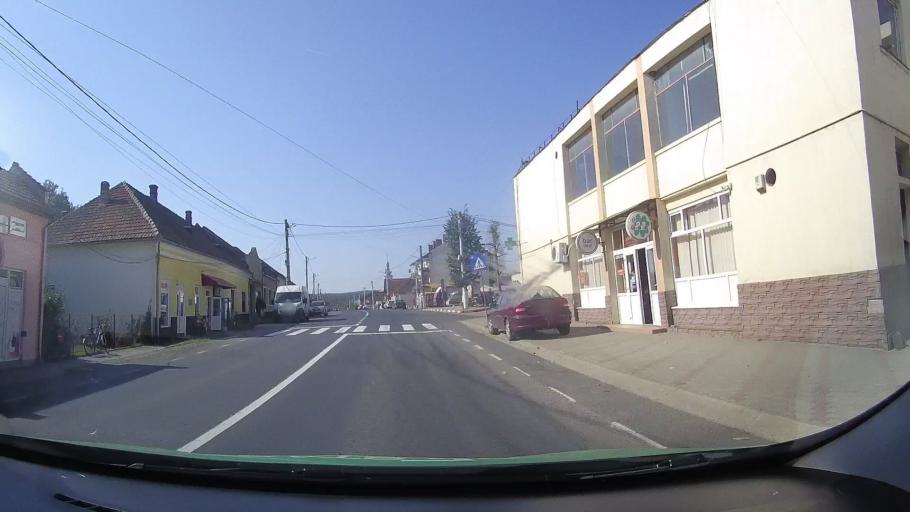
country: RO
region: Arad
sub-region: Comuna Savarsin
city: Savarsin
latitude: 46.0143
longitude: 22.2366
